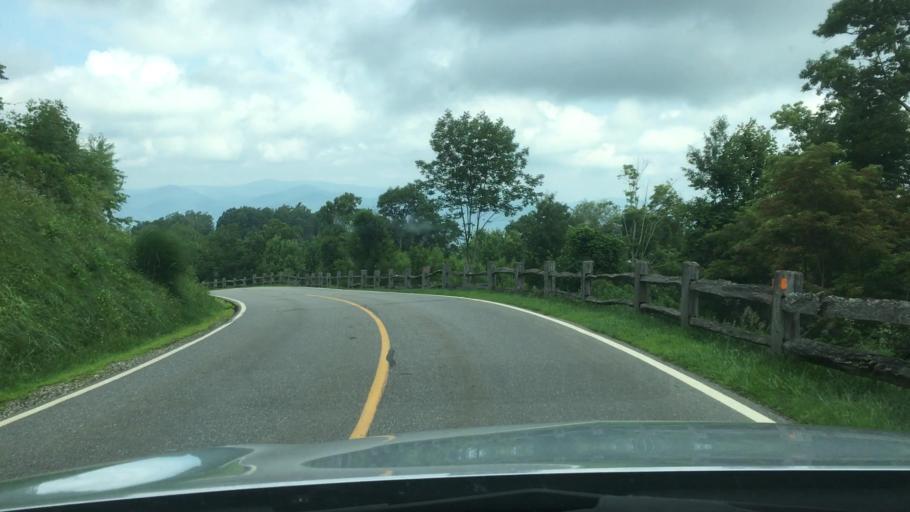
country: US
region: North Carolina
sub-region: Yancey County
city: Burnsville
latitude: 35.8751
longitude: -82.3456
